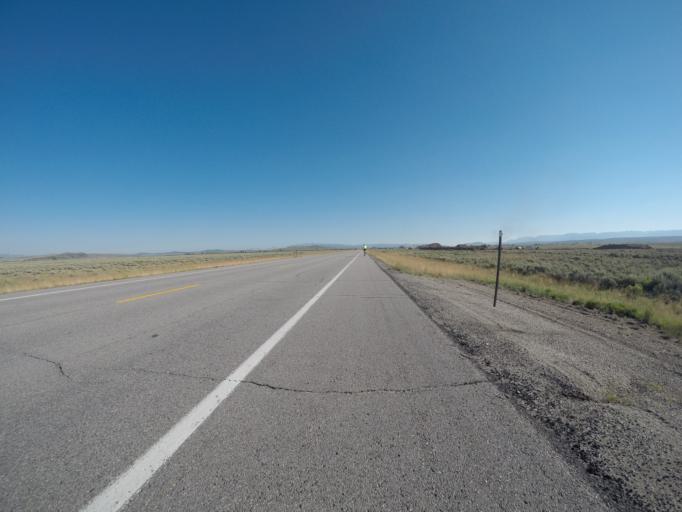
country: US
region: Wyoming
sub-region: Sublette County
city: Pinedale
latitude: 42.9658
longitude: -110.0888
